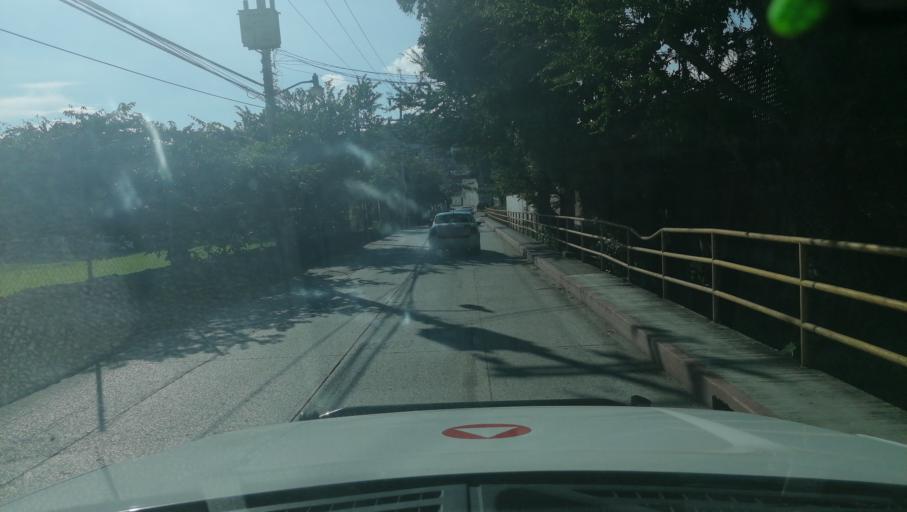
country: MX
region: Morelos
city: Emiliano Zapata
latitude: 18.8368
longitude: -99.1859
